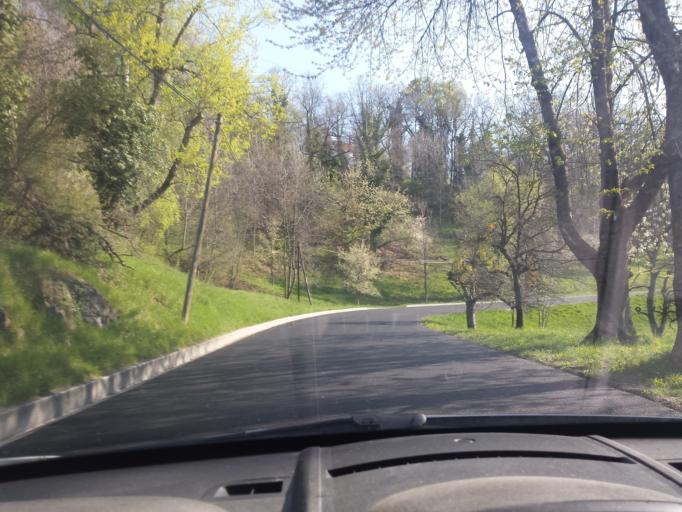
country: FR
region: Rhone-Alpes
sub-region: Departement de la Haute-Savoie
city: Passy
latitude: 45.9248
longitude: 6.6993
